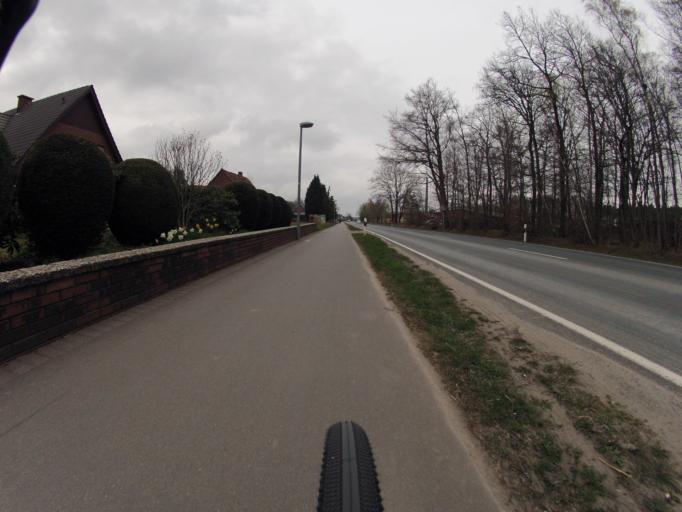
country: DE
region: North Rhine-Westphalia
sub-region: Regierungsbezirk Munster
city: Mettingen
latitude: 52.3364
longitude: 7.7425
